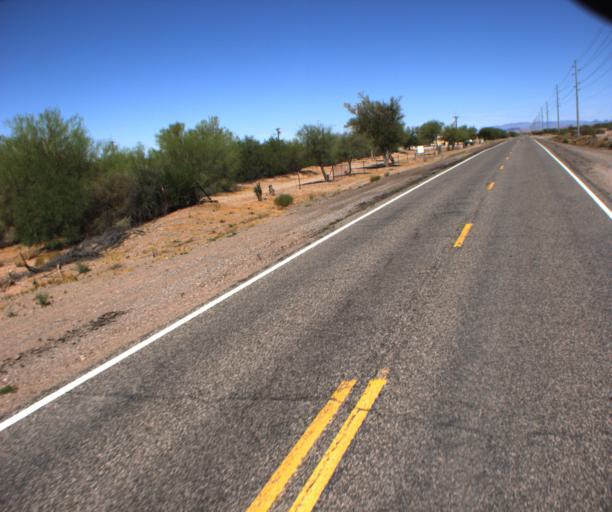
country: US
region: Arizona
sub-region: La Paz County
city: Cienega Springs
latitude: 33.9507
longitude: -114.0211
